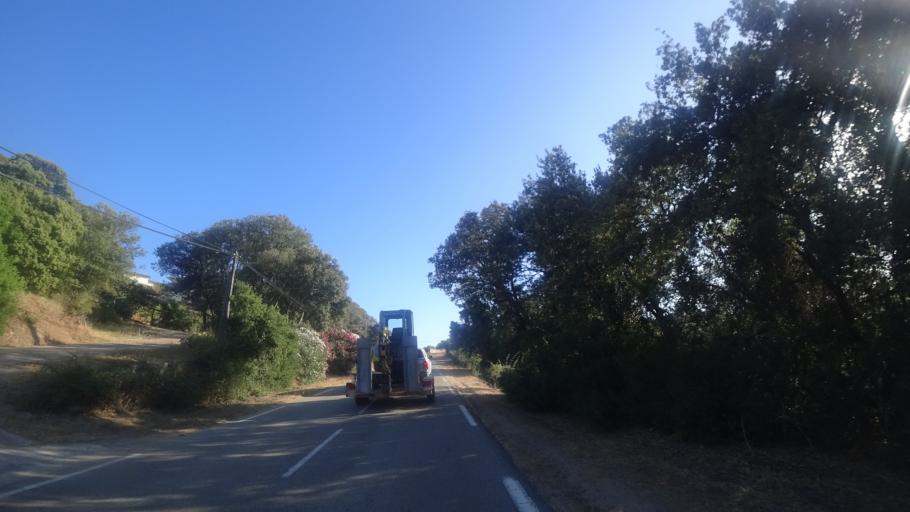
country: FR
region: Corsica
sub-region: Departement de la Corse-du-Sud
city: Cargese
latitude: 42.1482
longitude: 8.6037
